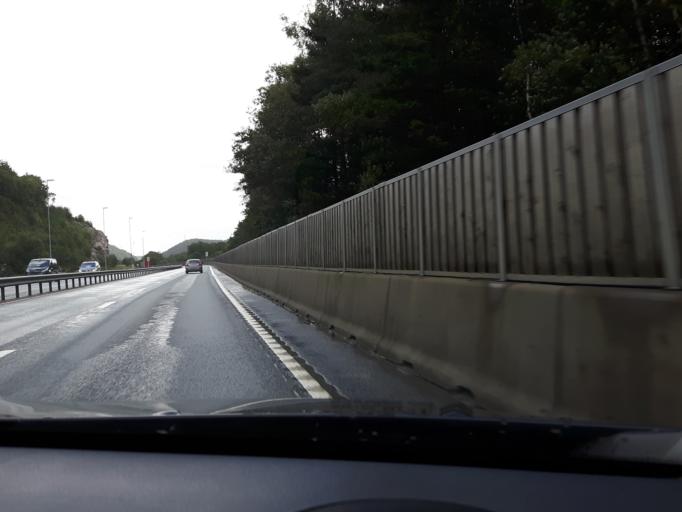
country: NO
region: Vest-Agder
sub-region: Sogne
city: Tangvall
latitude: 58.1131
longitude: 7.8349
